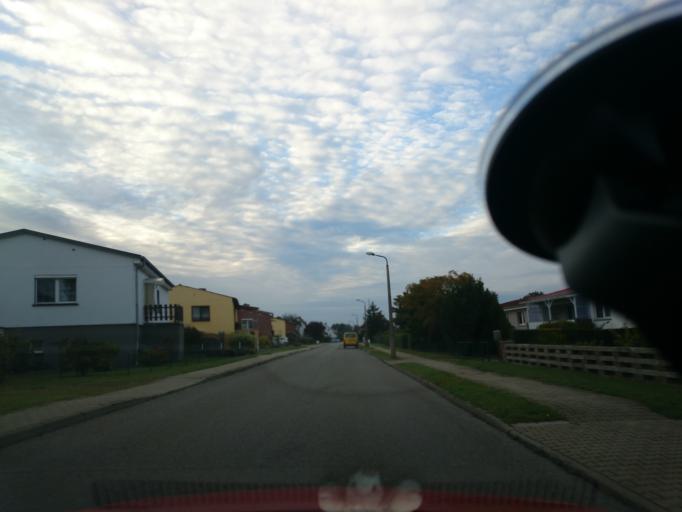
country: DE
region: Mecklenburg-Vorpommern
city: Barth
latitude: 54.3608
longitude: 12.7195
